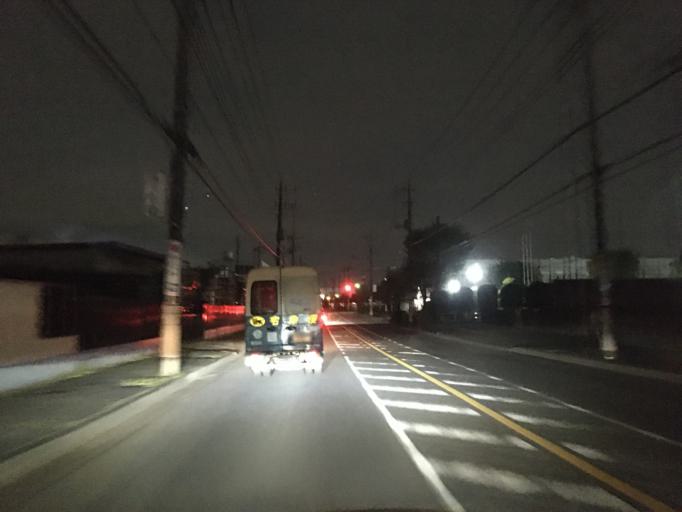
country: JP
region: Saitama
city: Sayama
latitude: 35.8734
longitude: 139.3917
